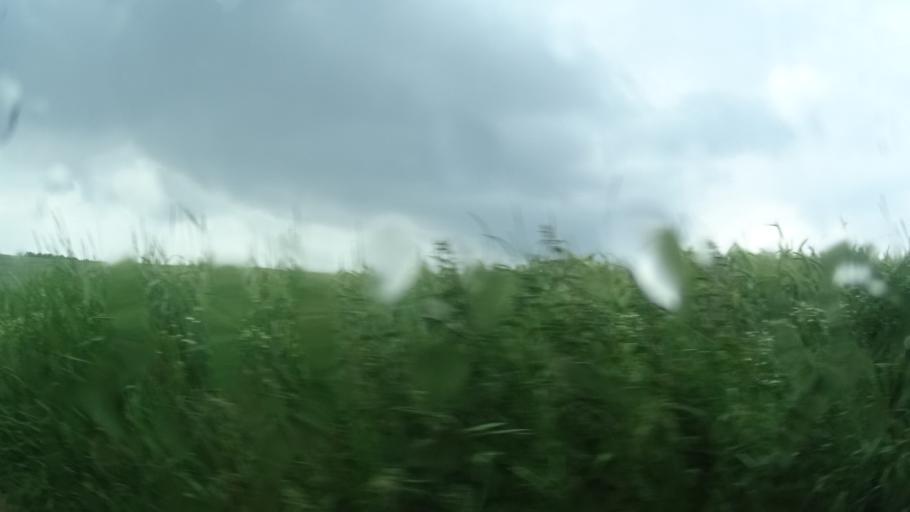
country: DE
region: Hesse
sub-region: Regierungsbezirk Giessen
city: Schlitz
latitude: 50.6696
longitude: 9.5363
